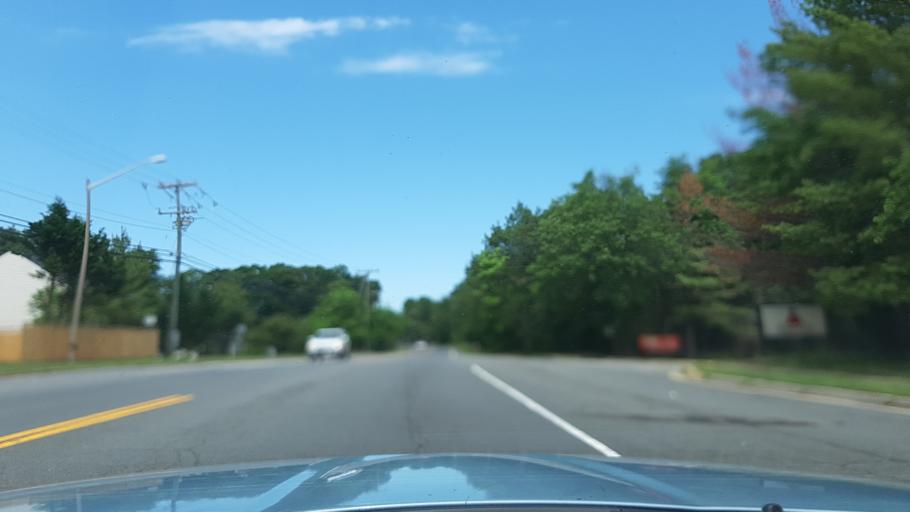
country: US
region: Virginia
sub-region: Fairfax County
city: Newington
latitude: 38.7365
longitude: -77.2097
